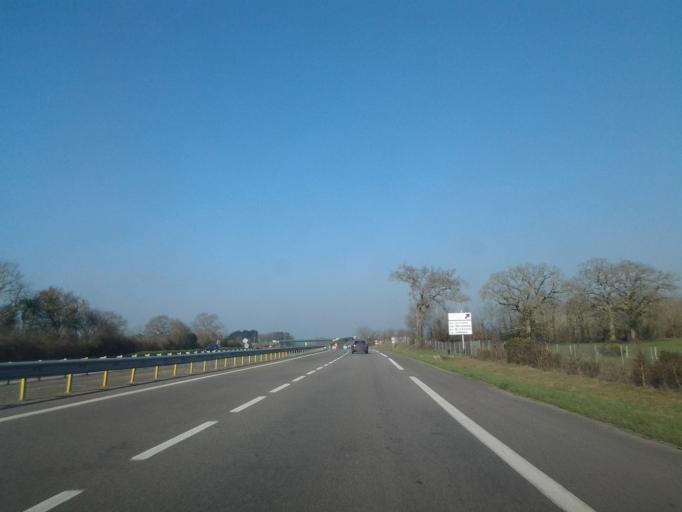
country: FR
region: Pays de la Loire
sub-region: Departement de la Vendee
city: Saint-Christophe-du-Ligneron
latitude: 46.7995
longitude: -1.7239
